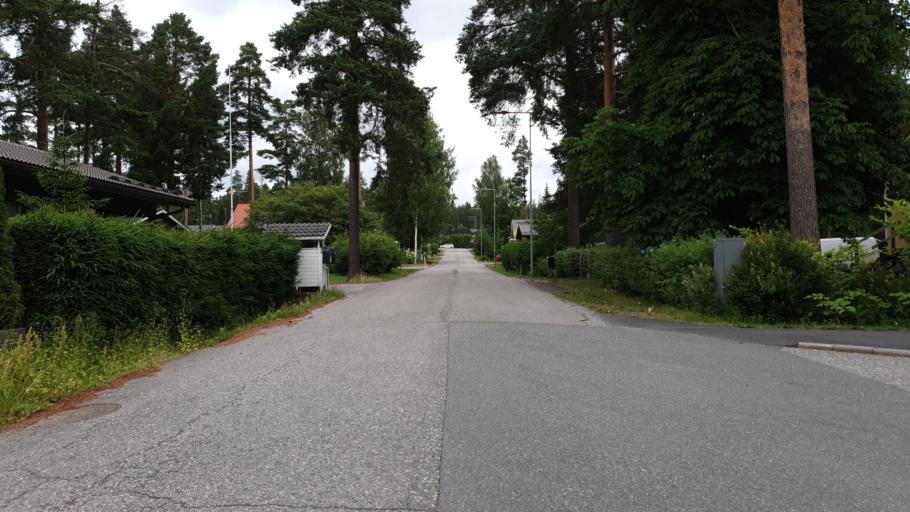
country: FI
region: Uusimaa
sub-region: Helsinki
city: Teekkarikylae
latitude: 60.2843
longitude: 24.9025
